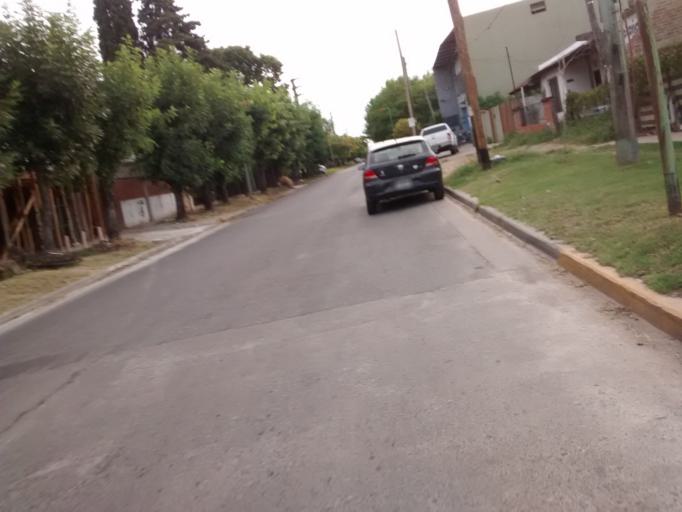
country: AR
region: Buenos Aires
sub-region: Partido de La Plata
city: La Plata
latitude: -34.8756
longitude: -58.0605
